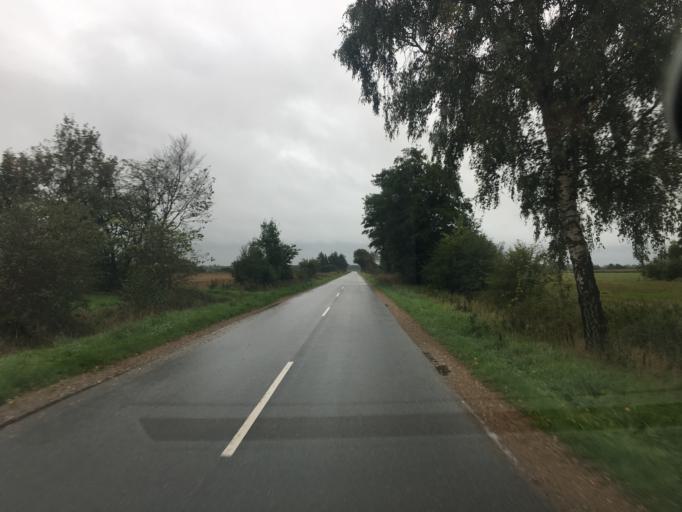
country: DK
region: South Denmark
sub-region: Tonder Kommune
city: Logumkloster
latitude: 54.9751
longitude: 9.0420
